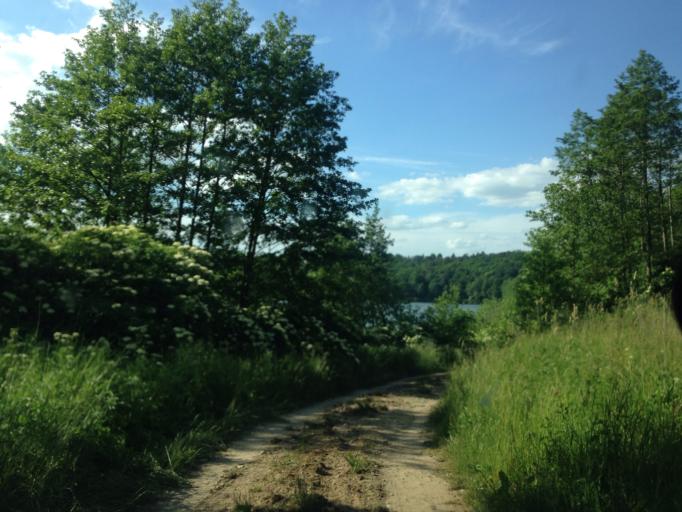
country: PL
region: Kujawsko-Pomorskie
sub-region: Powiat brodnicki
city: Brzozie
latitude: 53.3141
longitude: 19.5674
